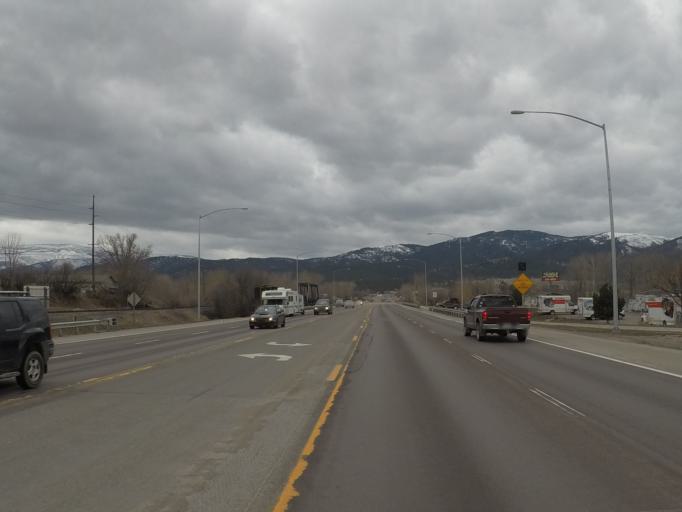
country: US
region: Montana
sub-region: Missoula County
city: Orchard Homes
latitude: 46.8325
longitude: -114.0516
